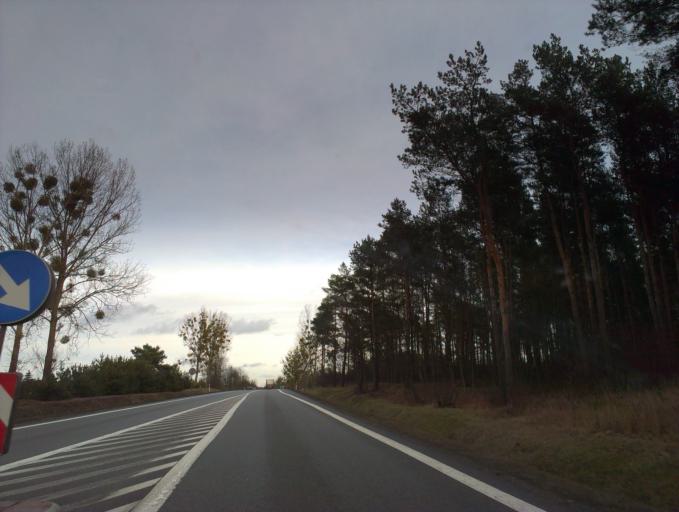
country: PL
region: Kujawsko-Pomorskie
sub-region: Powiat lipnowski
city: Skepe
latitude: 52.8775
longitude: 19.3729
